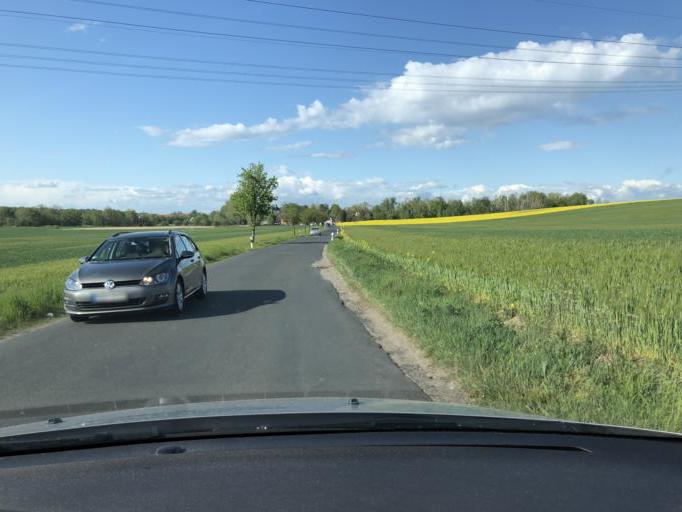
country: DE
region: Thuringia
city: Gerstenberg
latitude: 51.0211
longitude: 12.4399
